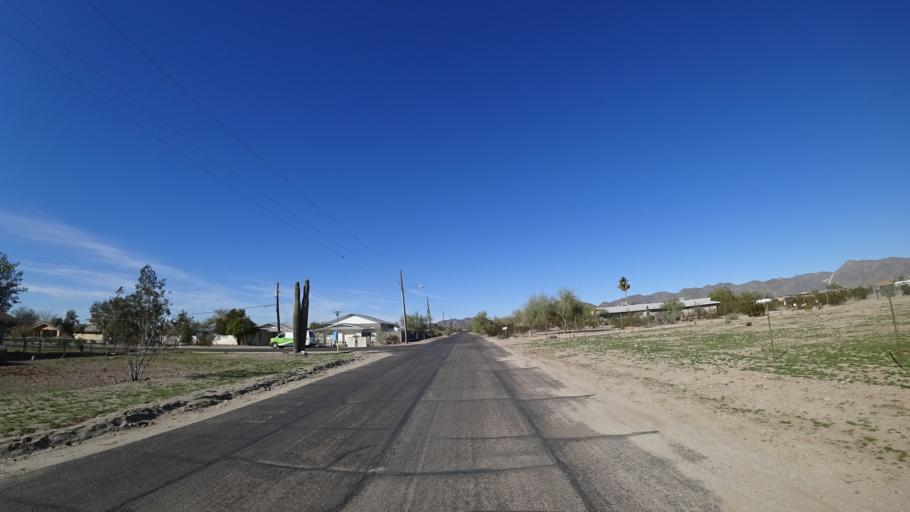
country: US
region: Arizona
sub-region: Maricopa County
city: Citrus Park
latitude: 33.4720
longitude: -112.4893
